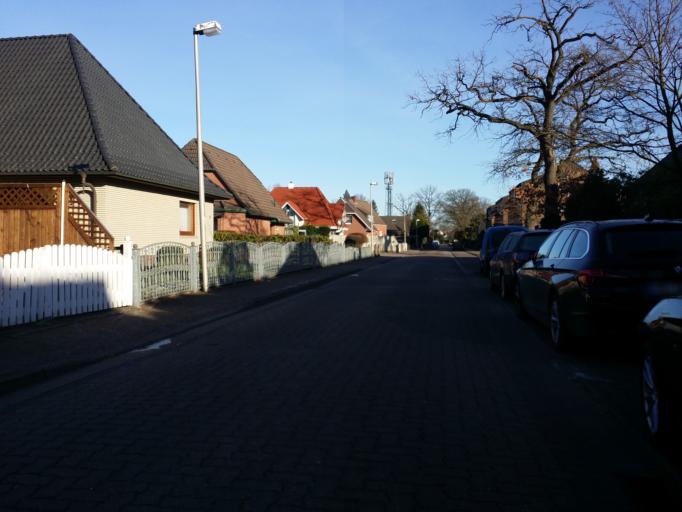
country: DE
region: Lower Saxony
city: Delmenhorst
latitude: 53.0553
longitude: 8.6746
